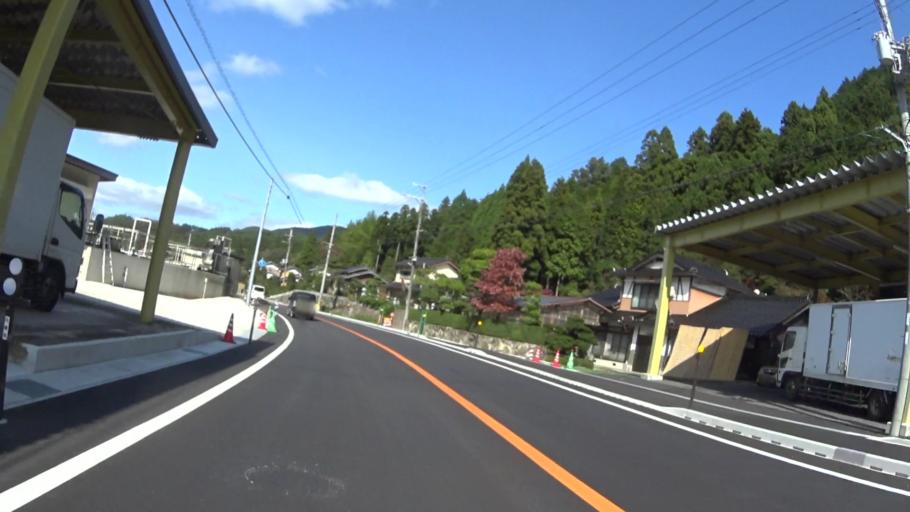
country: JP
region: Kyoto
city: Fukuchiyama
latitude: 35.4231
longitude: 135.0074
